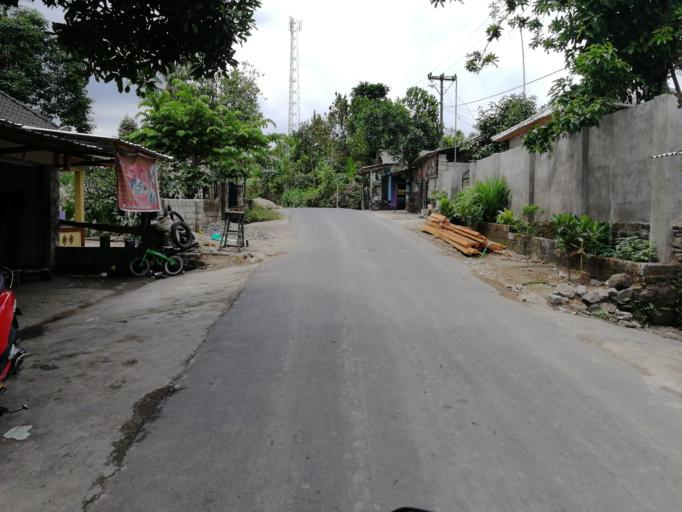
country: ID
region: West Nusa Tenggara
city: Pediti
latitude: -8.5670
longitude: 116.3307
